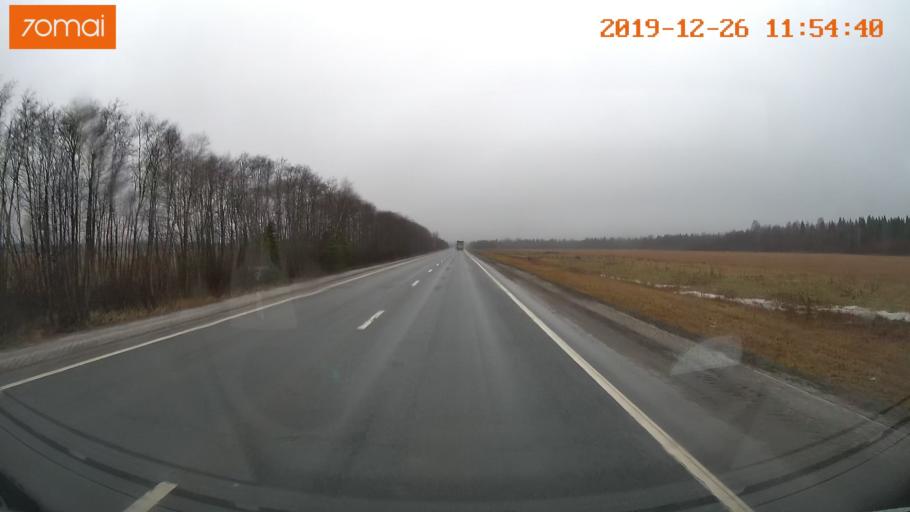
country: RU
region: Vologda
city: Sheksna
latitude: 59.2770
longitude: 38.3003
